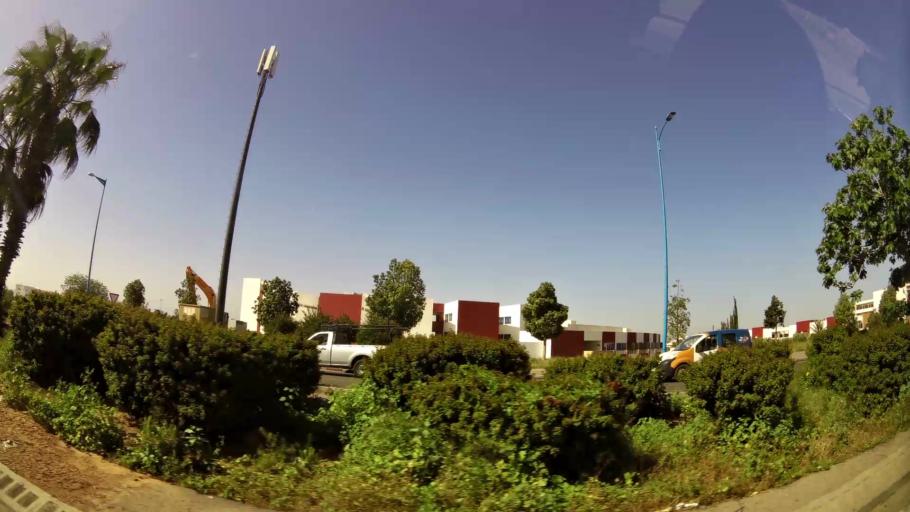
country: MA
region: Oued ed Dahab-Lagouira
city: Dakhla
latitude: 30.4108
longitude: -9.5412
